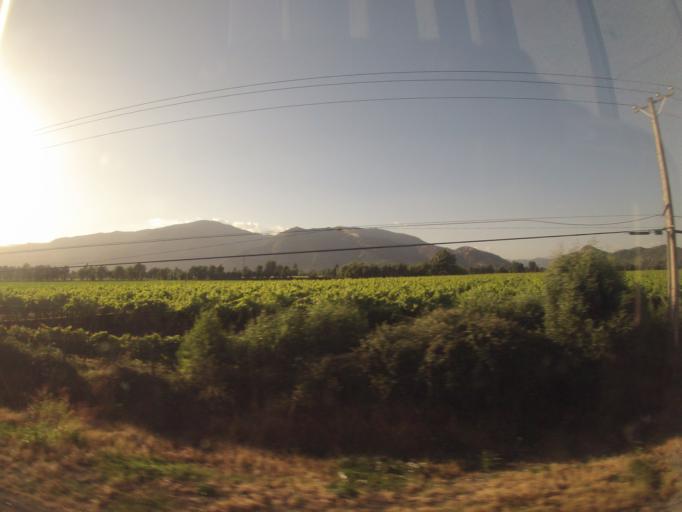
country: CL
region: O'Higgins
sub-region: Provincia de Cachapoal
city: San Vicente
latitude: -34.5490
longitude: -70.9578
